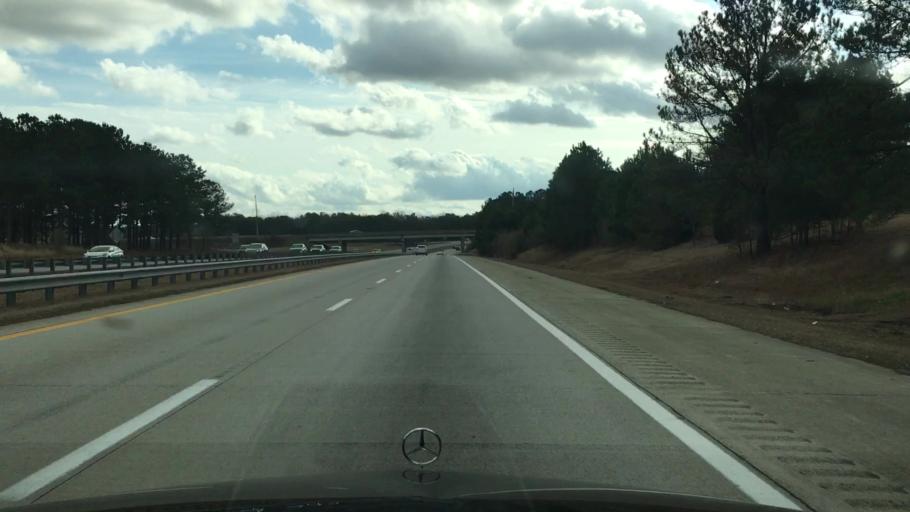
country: US
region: North Carolina
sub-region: Wake County
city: Garner
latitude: 35.6094
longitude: -78.5654
